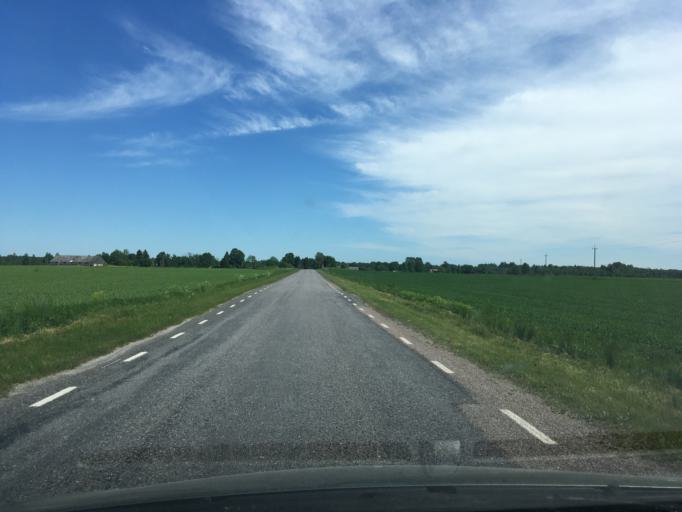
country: EE
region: Raplamaa
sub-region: Rapla vald
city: Rapla
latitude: 59.0446
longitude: 24.8700
